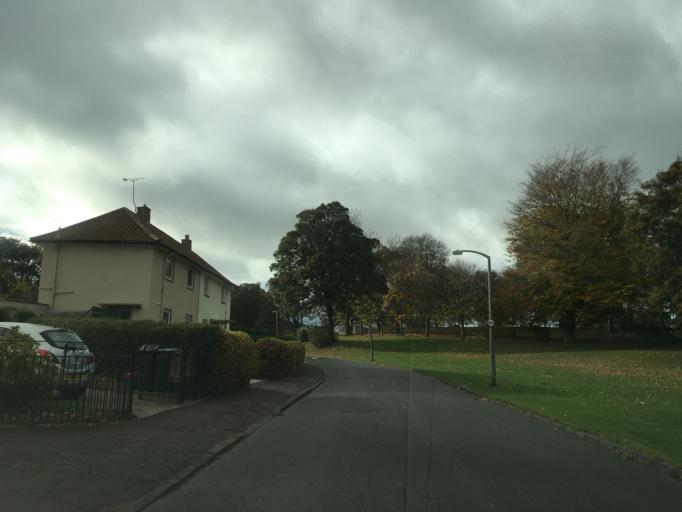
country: GB
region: Scotland
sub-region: Midlothian
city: Loanhead
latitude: 55.9230
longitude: -3.1593
